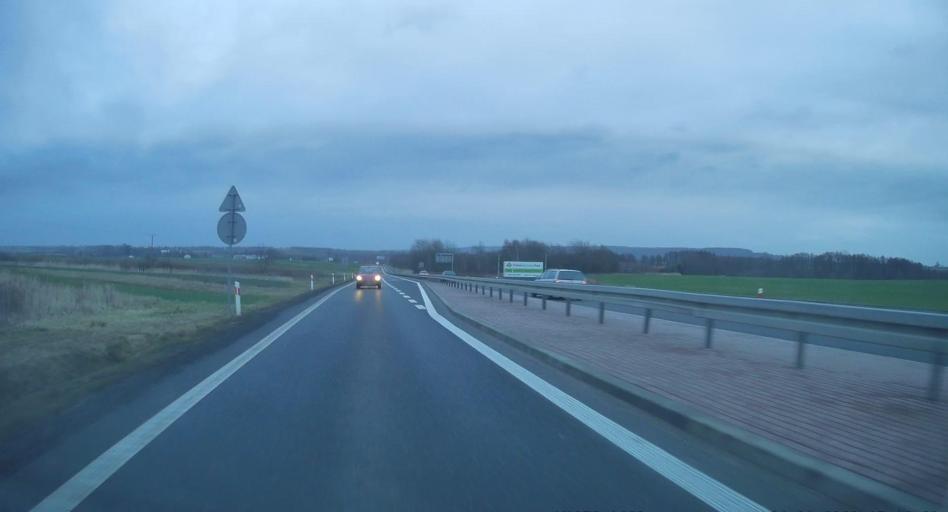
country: PL
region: Subcarpathian Voivodeship
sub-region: Powiat ropczycko-sedziszowski
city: Sedziszow Malopolski
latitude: 50.0625
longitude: 21.7166
